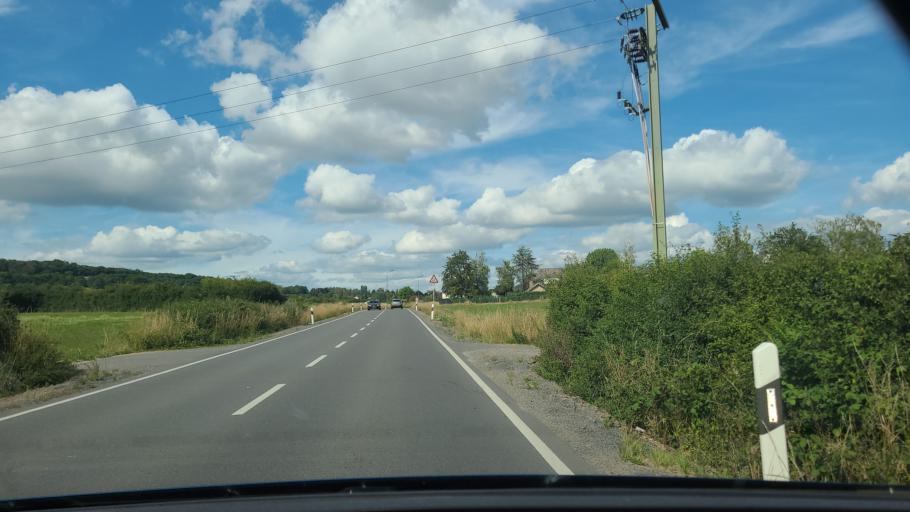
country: LU
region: Luxembourg
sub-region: Canton de Capellen
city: Bascharage
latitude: 49.5695
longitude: 5.8978
